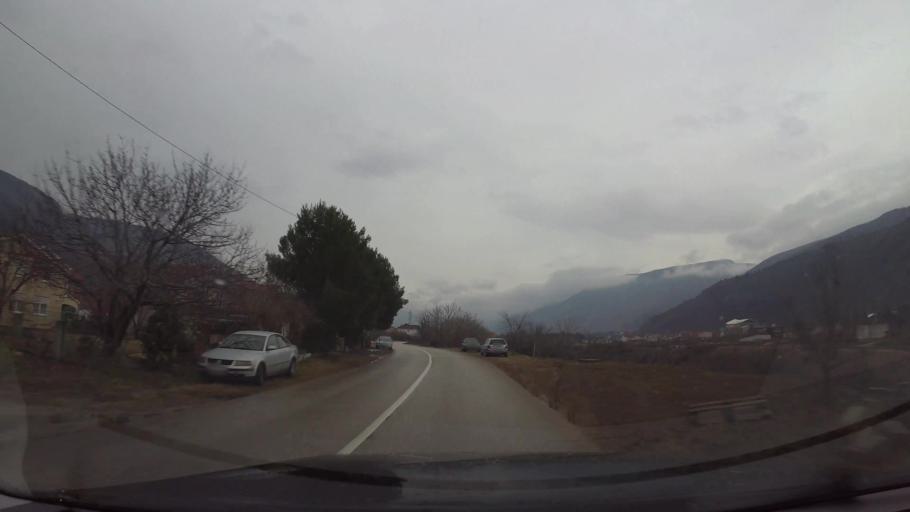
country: BA
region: Federation of Bosnia and Herzegovina
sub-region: Hercegovacko-Bosanski Kanton
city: Mostar
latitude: 43.3670
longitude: 17.8207
